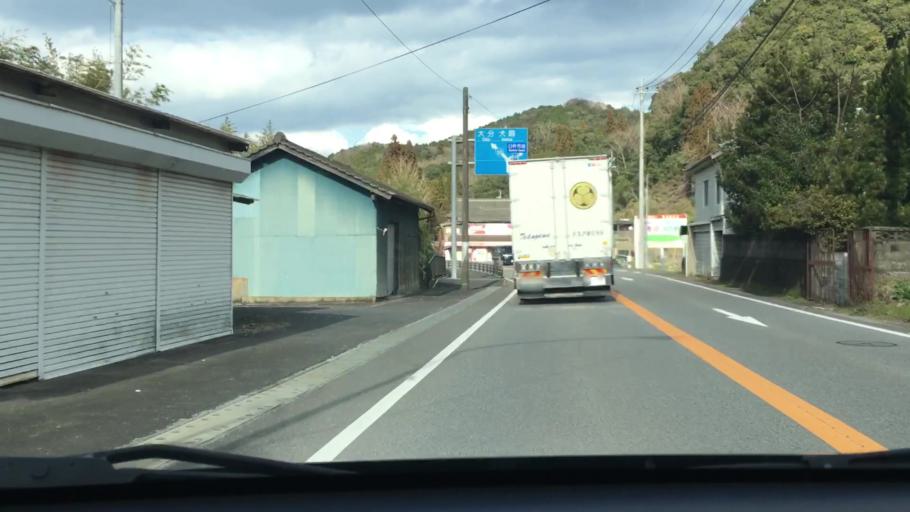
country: JP
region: Oita
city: Usuki
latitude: 33.0165
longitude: 131.7009
